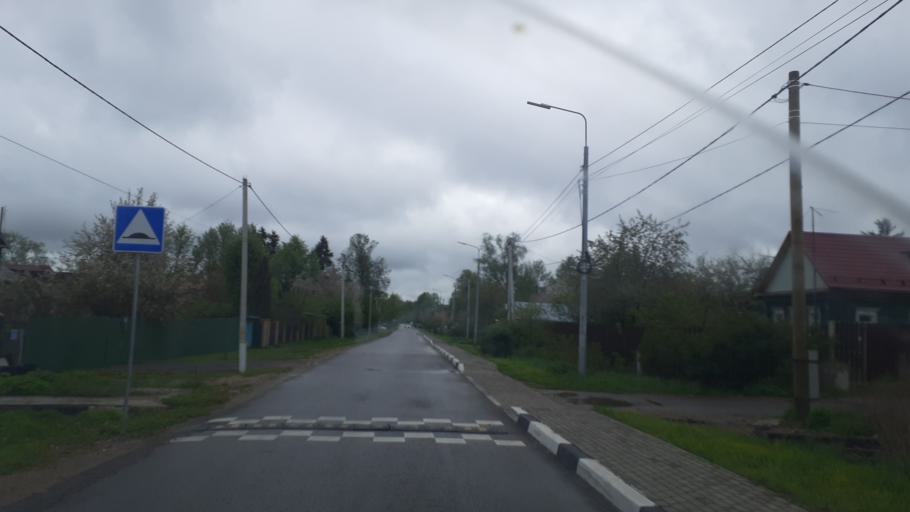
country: RU
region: Moskovskaya
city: Gorki Vtoryye
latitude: 55.7016
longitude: 37.2039
